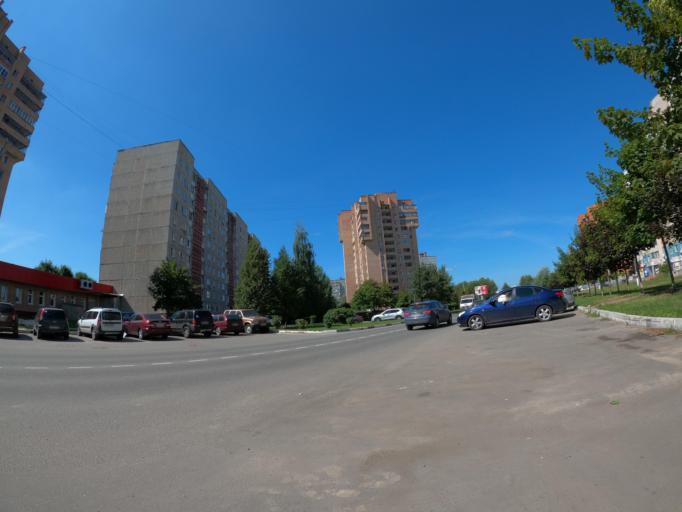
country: RU
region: Moskovskaya
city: Stupino
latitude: 54.8928
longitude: 38.0666
